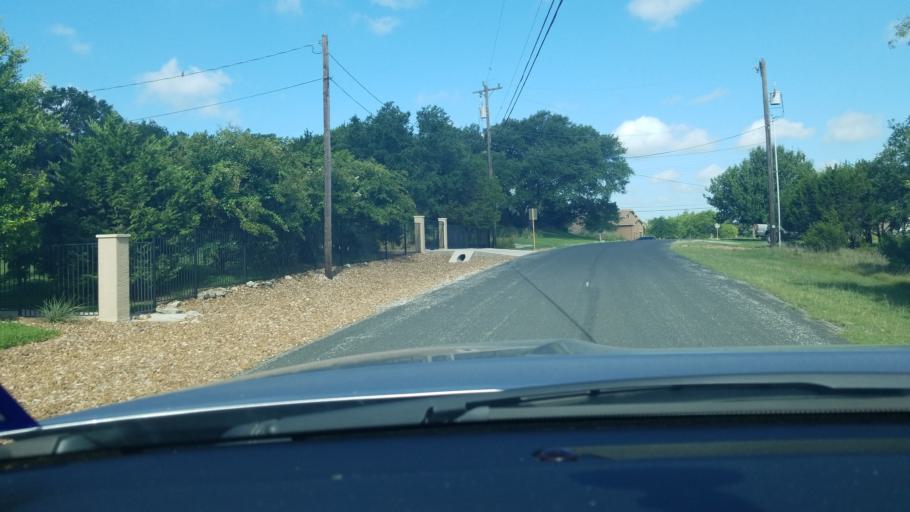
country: US
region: Texas
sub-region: Bexar County
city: Timberwood Park
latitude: 29.7053
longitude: -98.4888
